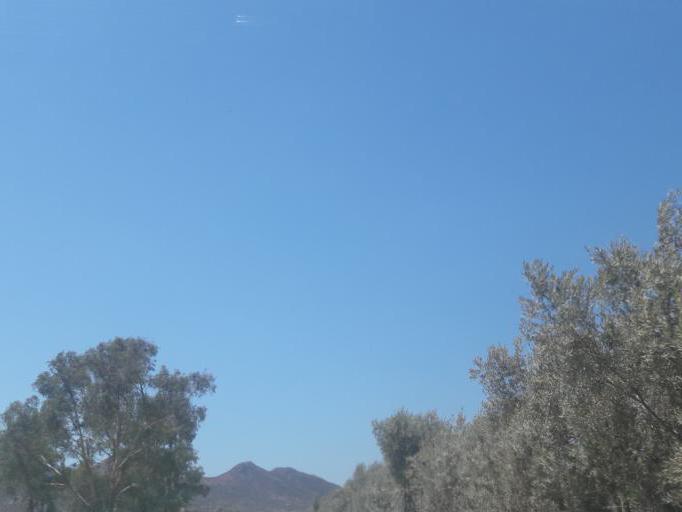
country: MX
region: Baja California
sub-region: Ensenada
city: Rancho Verde
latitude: 32.0867
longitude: -116.6267
